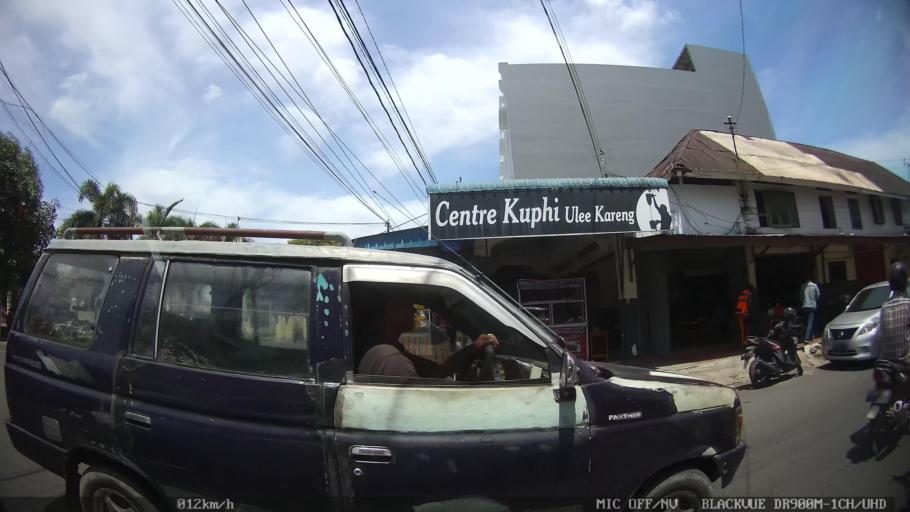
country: ID
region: North Sumatra
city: Binjai
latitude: 3.6008
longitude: 98.4858
